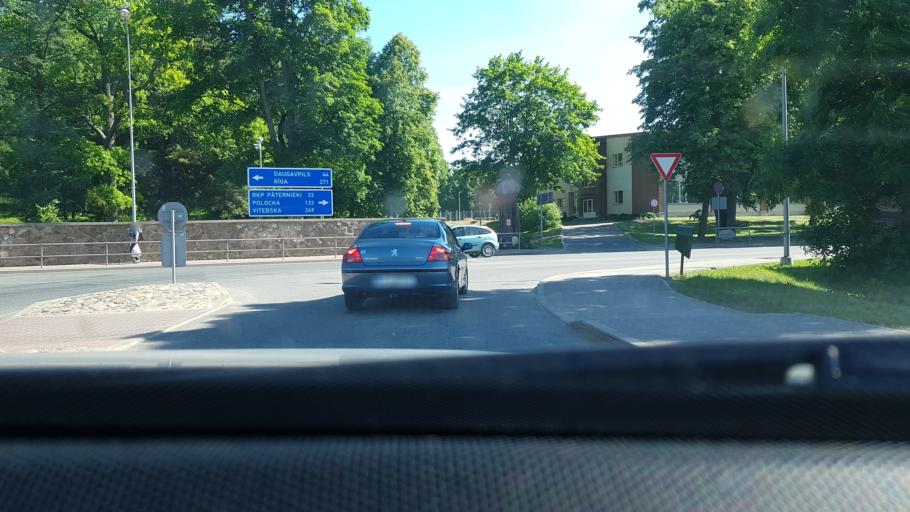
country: LV
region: Kraslavas Rajons
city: Kraslava
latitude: 55.8975
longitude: 27.1586
